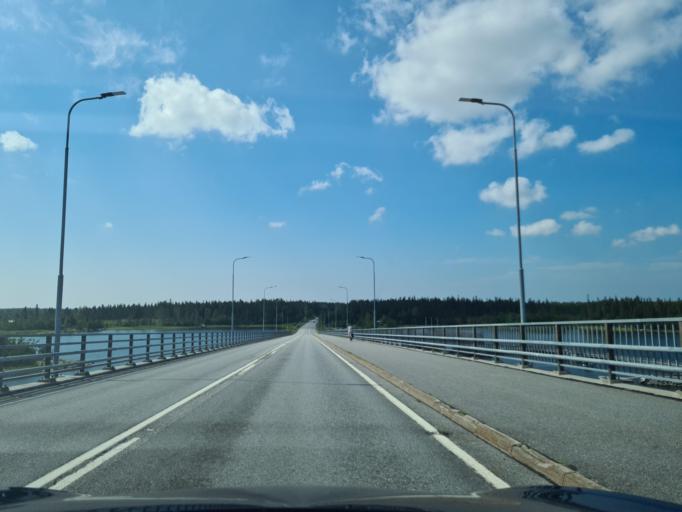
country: FI
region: Ostrobothnia
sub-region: Vaasa
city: Replot
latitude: 63.2066
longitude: 21.4659
